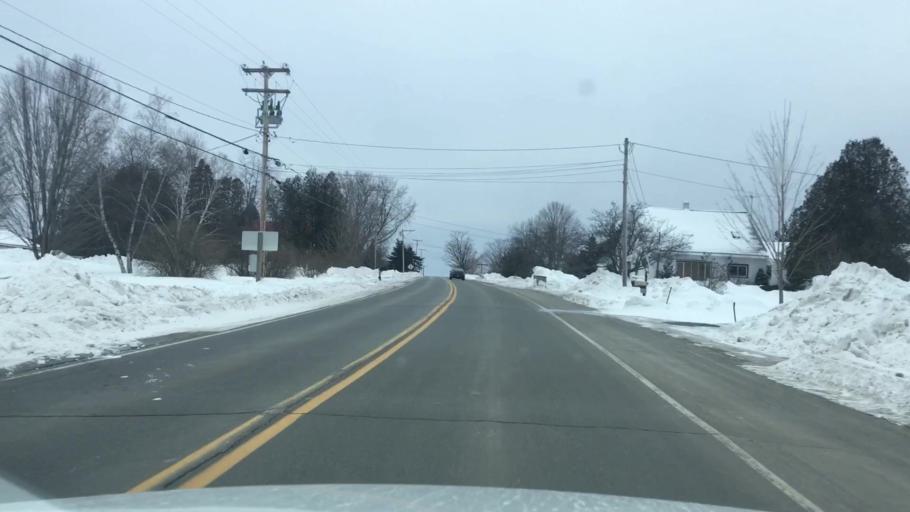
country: US
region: Maine
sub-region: Penobscot County
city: Charleston
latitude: 44.9953
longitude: -69.0541
